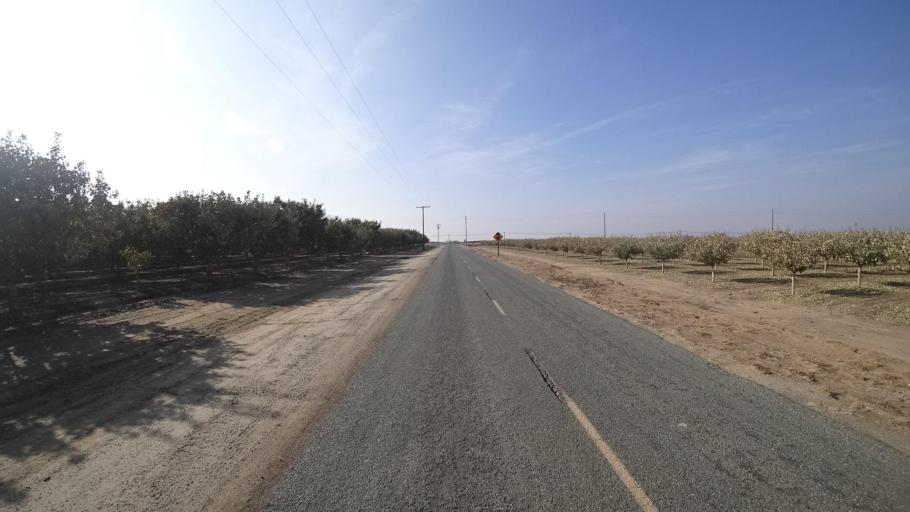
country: US
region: California
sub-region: Tulare County
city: Richgrove
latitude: 35.7907
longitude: -119.1124
